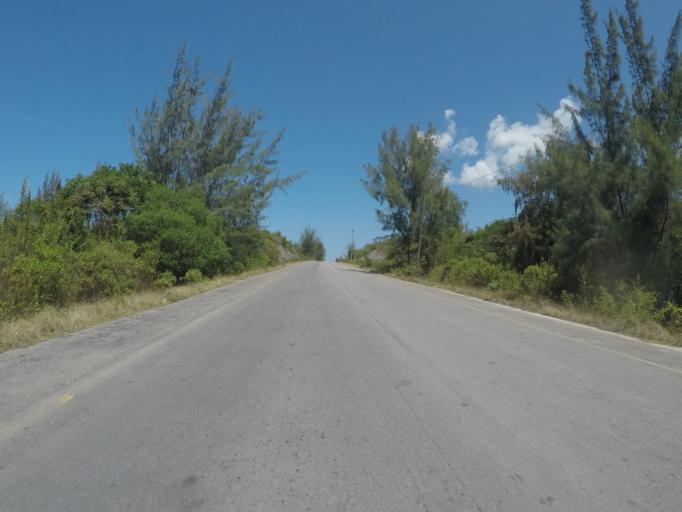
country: TZ
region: Zanzibar Central/South
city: Nganane
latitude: -6.2835
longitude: 39.5359
